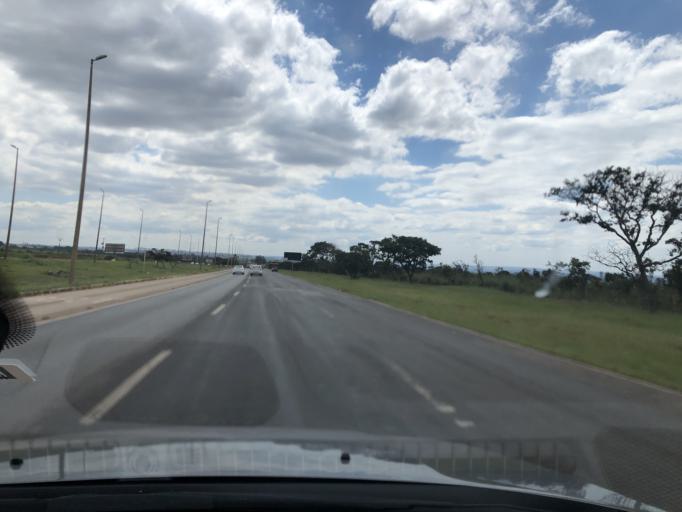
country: BR
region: Federal District
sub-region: Brasilia
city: Brasilia
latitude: -15.9697
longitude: -47.9910
